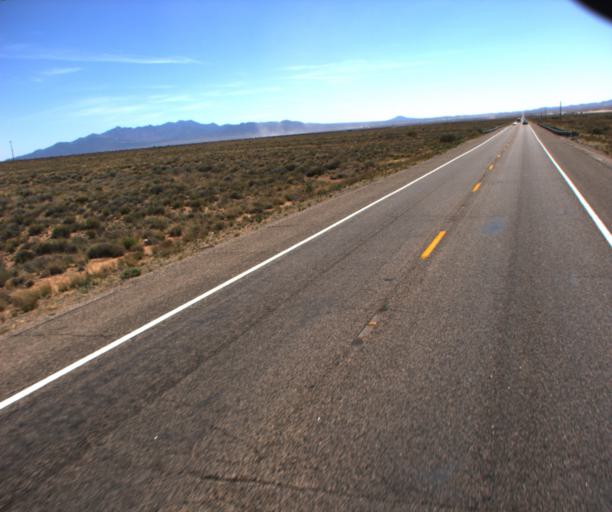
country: US
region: Arizona
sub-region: Mohave County
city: New Kingman-Butler
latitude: 35.3762
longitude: -113.8585
